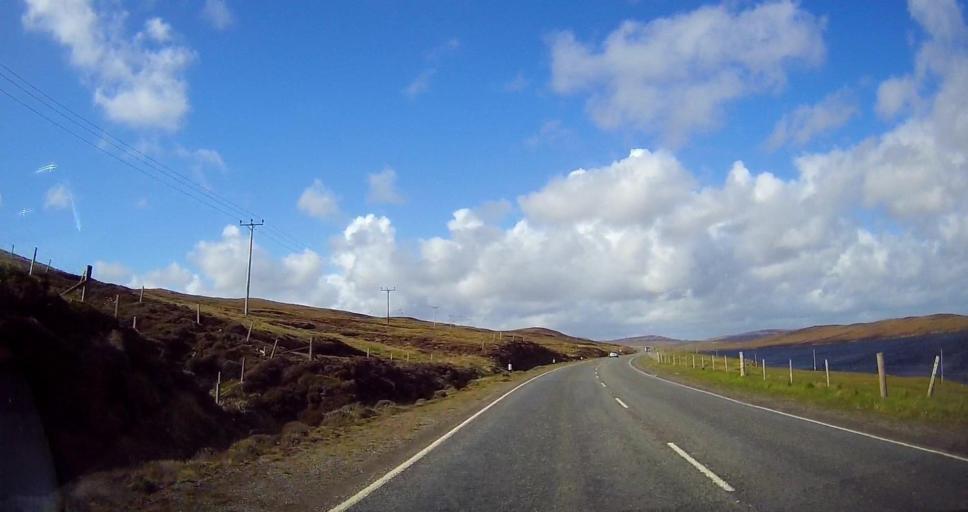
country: GB
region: Scotland
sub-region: Shetland Islands
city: Lerwick
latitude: 60.2452
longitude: -1.2286
